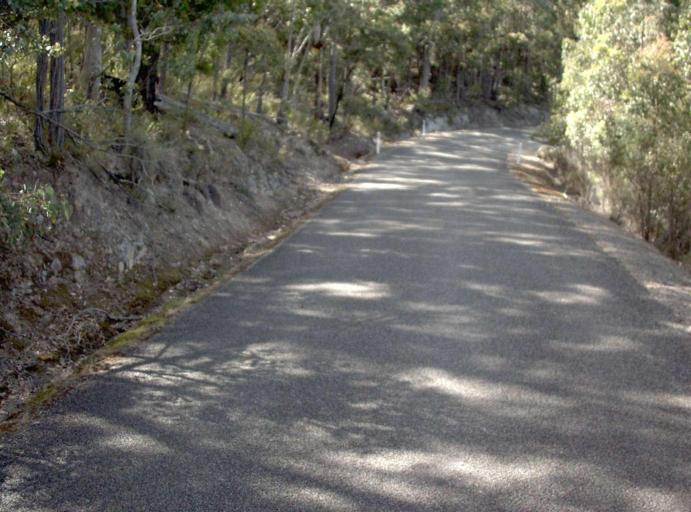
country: AU
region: Victoria
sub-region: East Gippsland
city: Lakes Entrance
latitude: -37.4772
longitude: 148.1245
